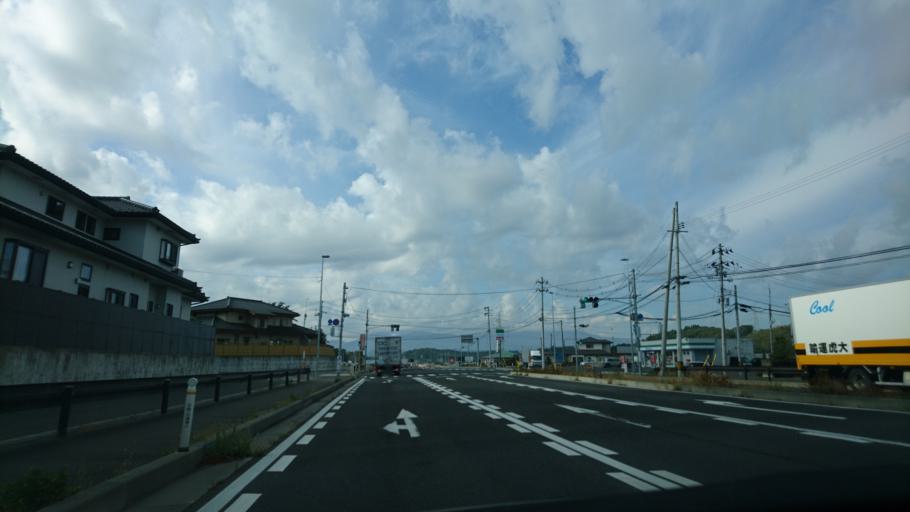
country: JP
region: Miyagi
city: Furukawa
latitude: 38.5186
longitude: 140.9090
